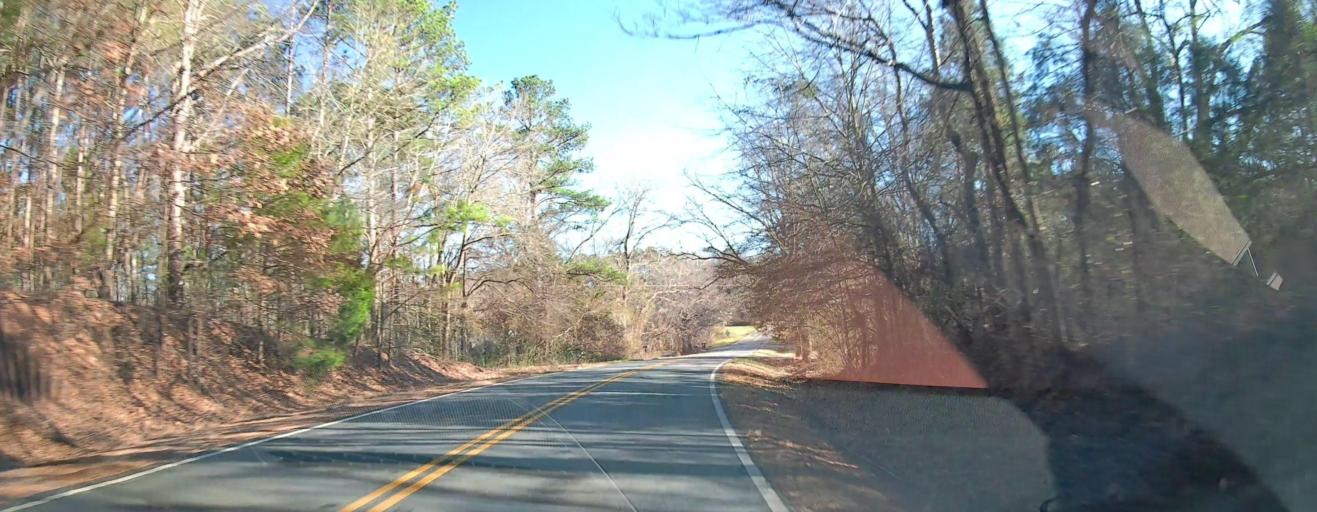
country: US
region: Georgia
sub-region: Meriwether County
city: Manchester
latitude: 32.9381
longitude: -84.6370
